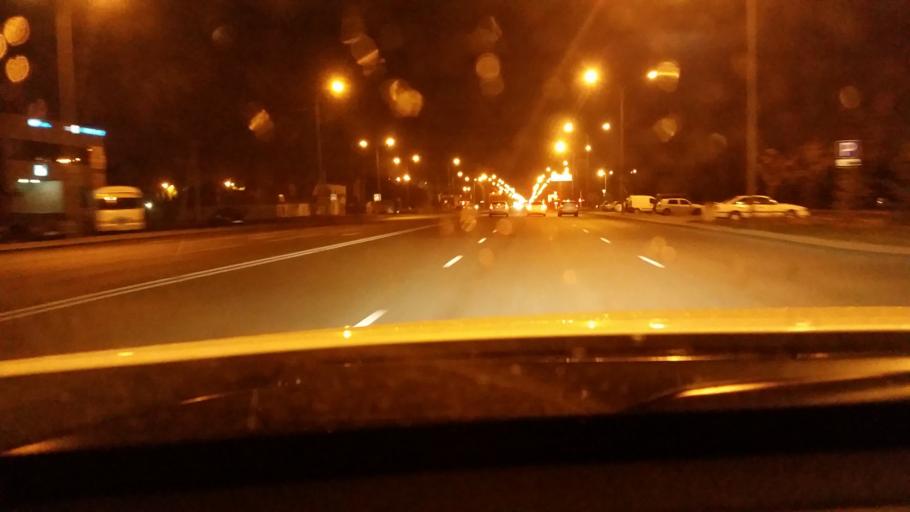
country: KZ
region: Astana Qalasy
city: Astana
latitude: 51.1405
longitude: 71.4891
